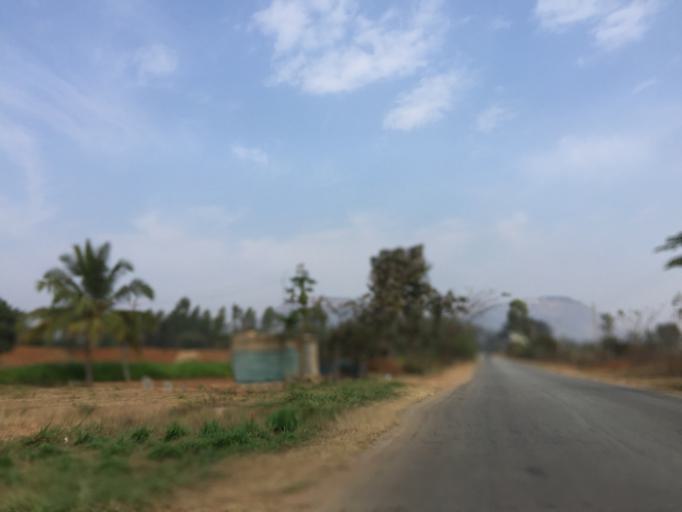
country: IN
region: Karnataka
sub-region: Bangalore Rural
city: Devanhalli
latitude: 13.3212
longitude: 77.6938
